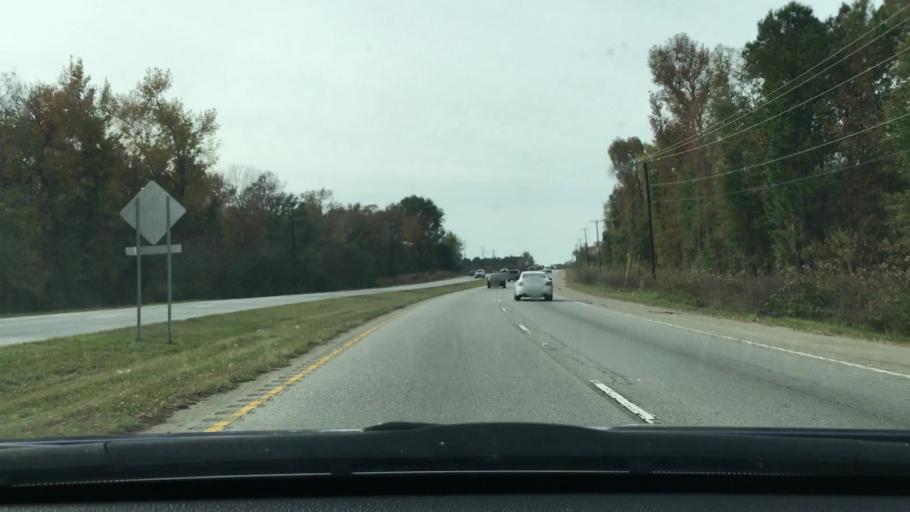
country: US
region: South Carolina
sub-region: Richland County
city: Hopkins
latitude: 33.9444
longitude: -80.8756
